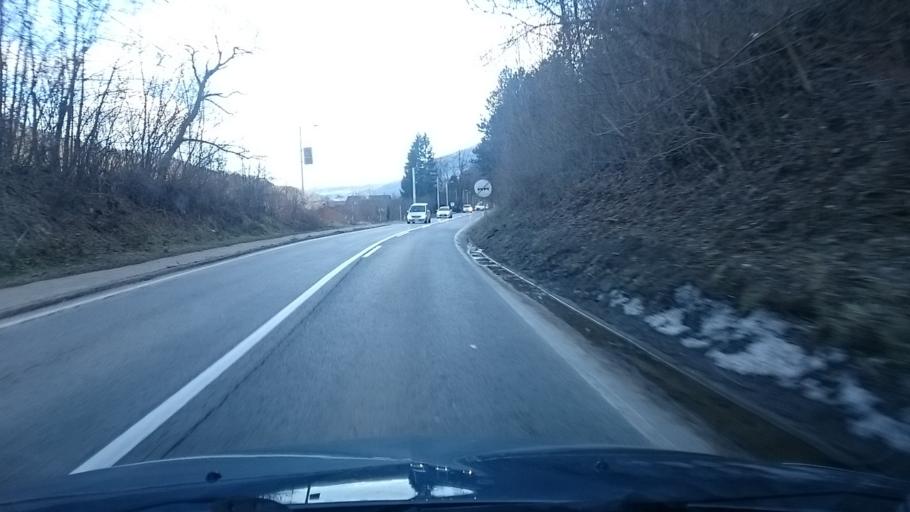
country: BA
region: Republika Srpska
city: Hiseti
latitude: 44.7287
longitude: 17.1535
